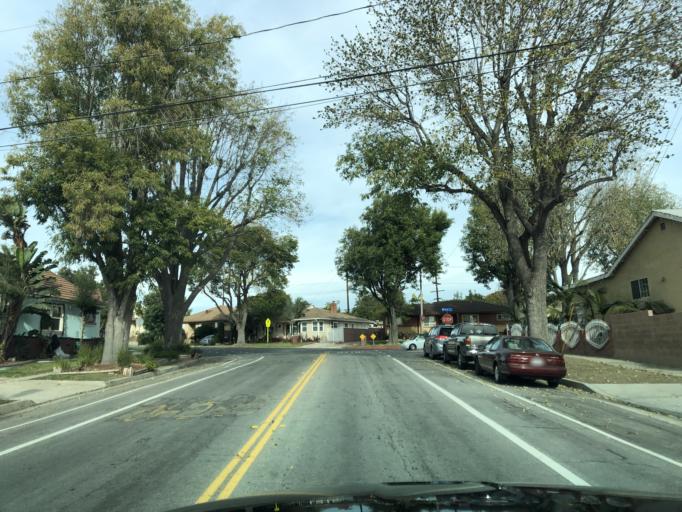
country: US
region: California
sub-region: Los Angeles County
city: Ladera Heights
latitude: 33.9808
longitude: -118.3664
